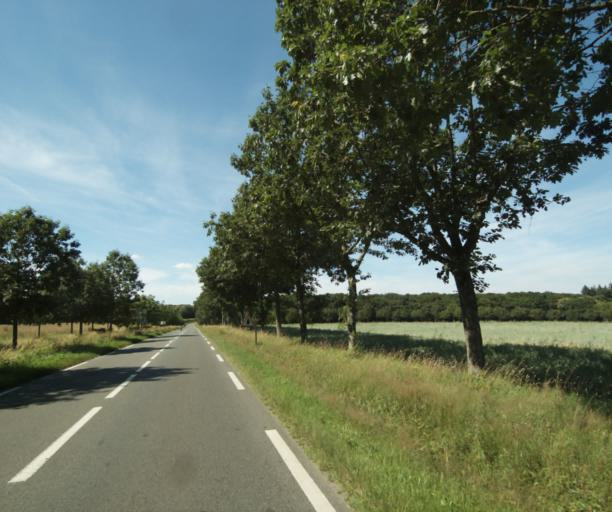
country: FR
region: Pays de la Loire
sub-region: Departement de la Mayenne
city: Laval
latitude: 48.0308
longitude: -0.7749
